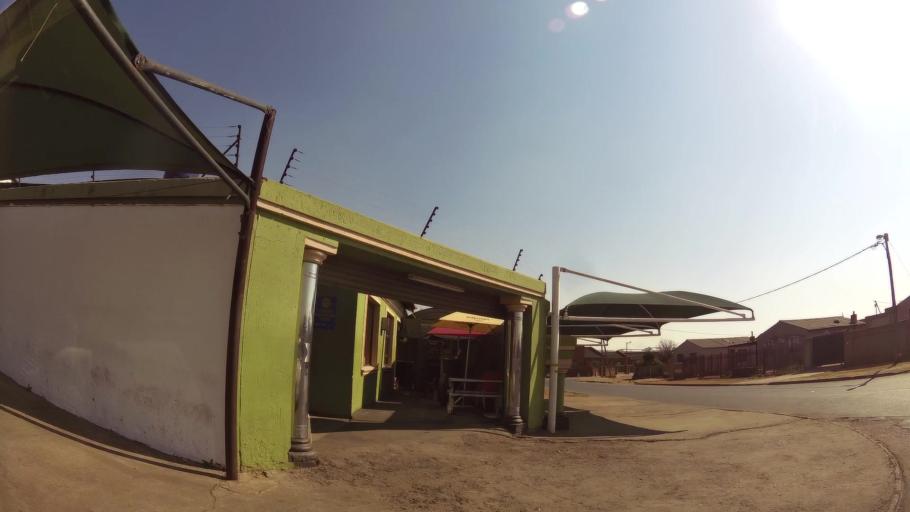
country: ZA
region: Gauteng
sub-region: Ekurhuleni Metropolitan Municipality
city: Boksburg
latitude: -26.2254
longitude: 28.2978
